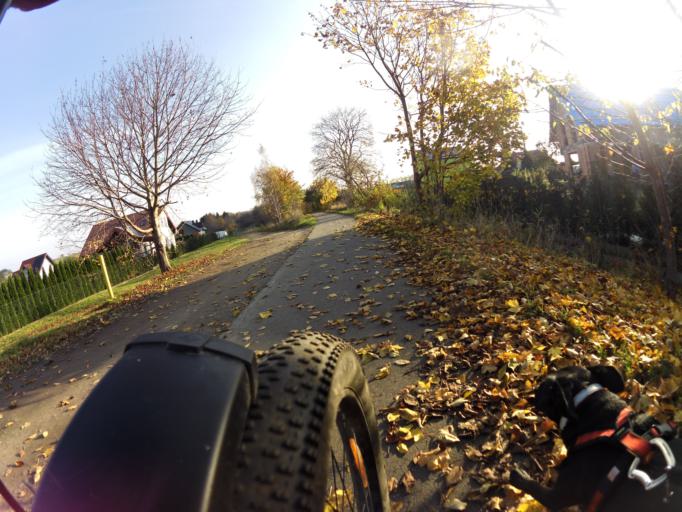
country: PL
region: Pomeranian Voivodeship
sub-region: Powiat pucki
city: Krokowa
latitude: 54.7814
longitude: 18.1632
